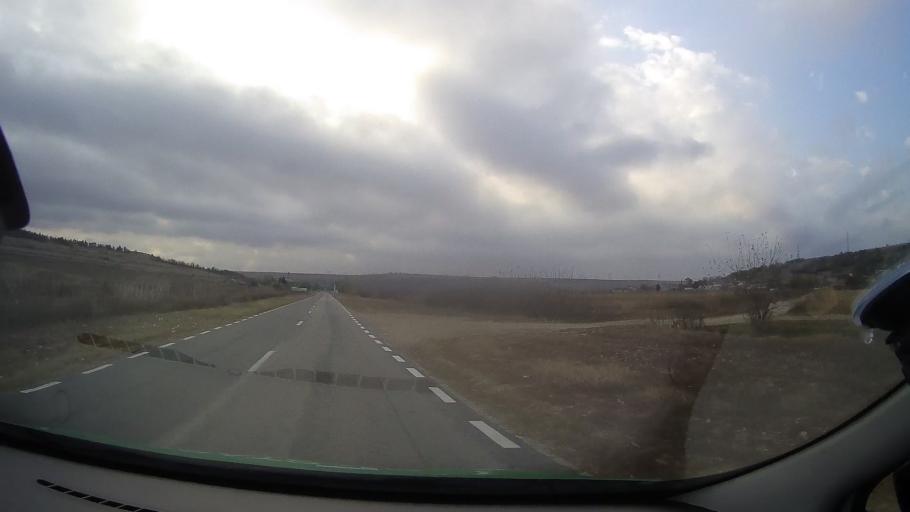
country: RO
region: Constanta
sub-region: Comuna Pestera
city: Pestera
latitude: 44.1968
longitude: 28.1316
